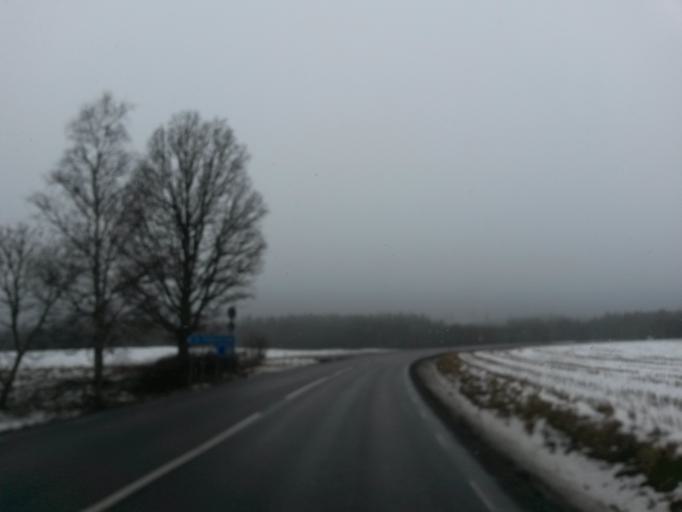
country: SE
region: Vaestra Goetaland
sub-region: Ulricehamns Kommun
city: Ulricehamn
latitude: 57.6667
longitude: 13.4017
